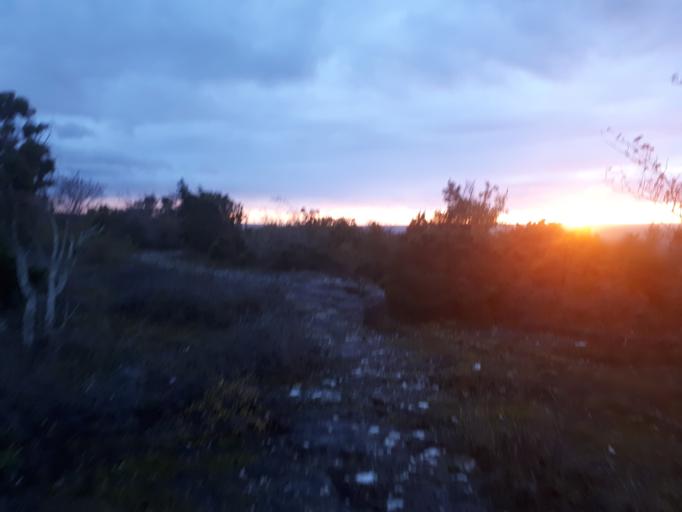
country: SE
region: Gotland
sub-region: Gotland
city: Visby
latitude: 57.6835
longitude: 18.3468
